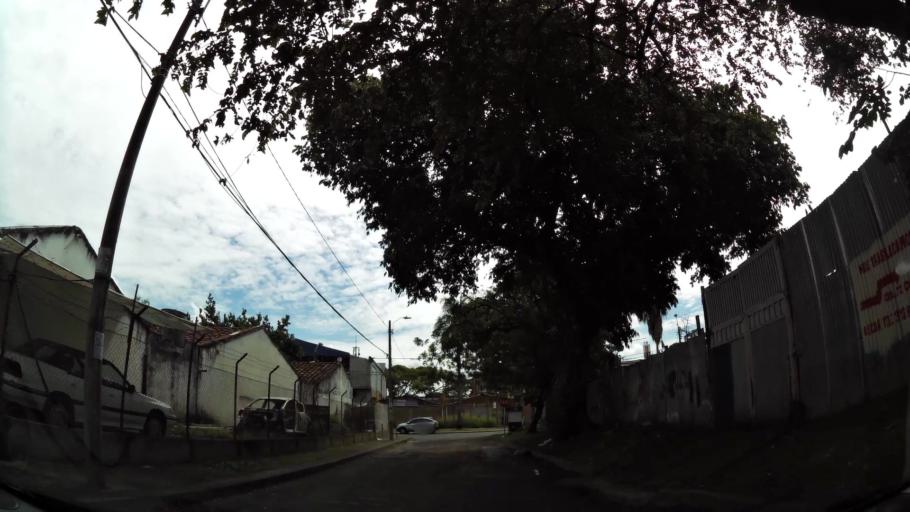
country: CO
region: Valle del Cauca
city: Cali
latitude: 3.3935
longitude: -76.5468
